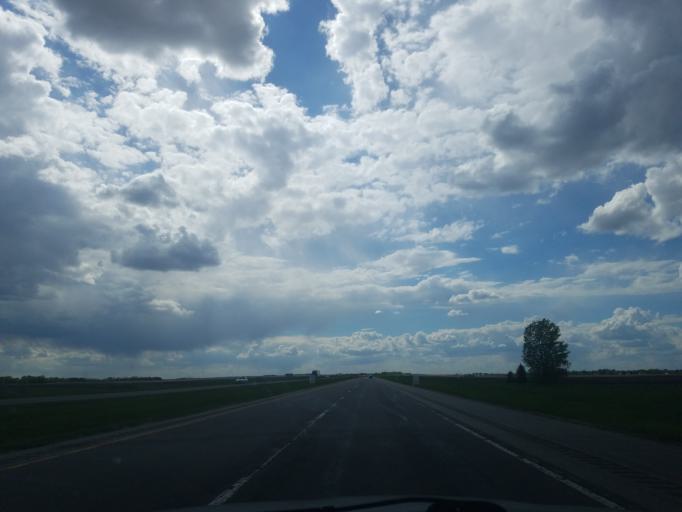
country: US
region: North Dakota
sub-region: Barnes County
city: Valley City
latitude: 46.9200
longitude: -97.7640
